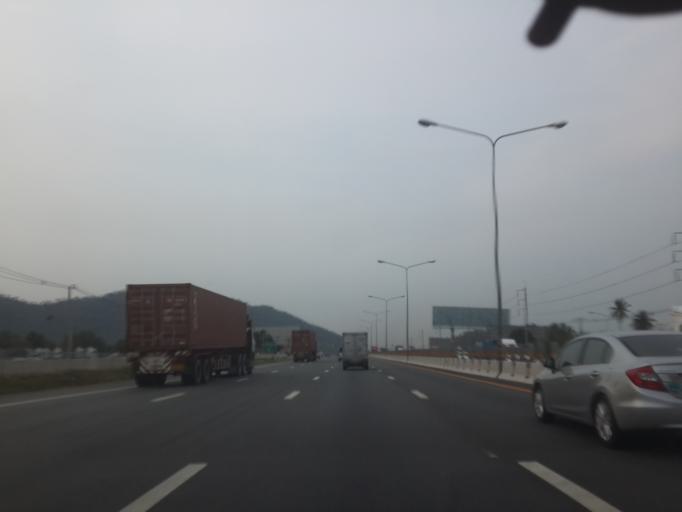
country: TH
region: Chon Buri
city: Si Racha
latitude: 13.2485
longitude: 100.9938
